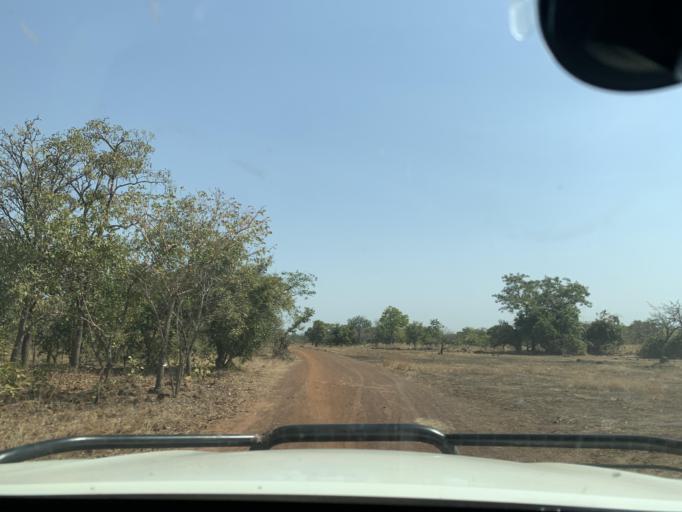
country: ML
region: Sikasso
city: Kolondieba
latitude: 10.8344
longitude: -6.7883
